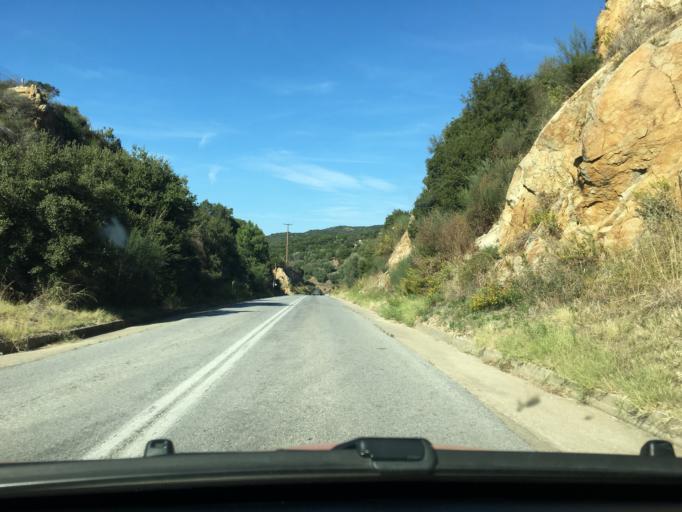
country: GR
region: Central Macedonia
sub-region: Nomos Chalkidikis
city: Ouranoupolis
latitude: 40.3344
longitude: 23.9728
